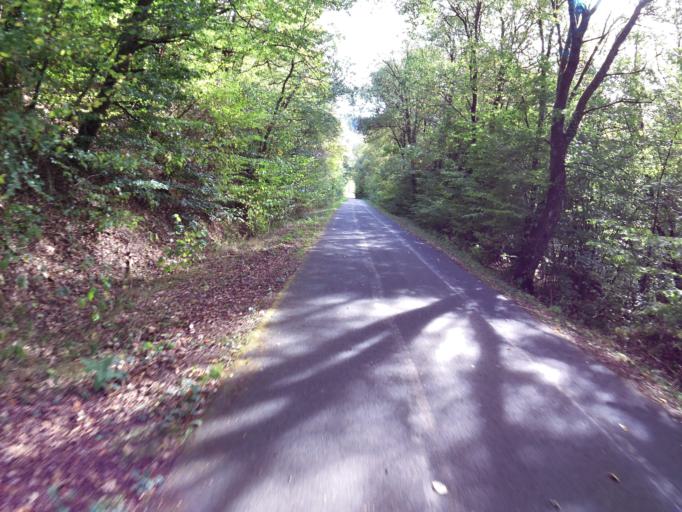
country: DE
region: Rheinland-Pfalz
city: Winterscheid
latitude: 50.2321
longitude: 6.2604
